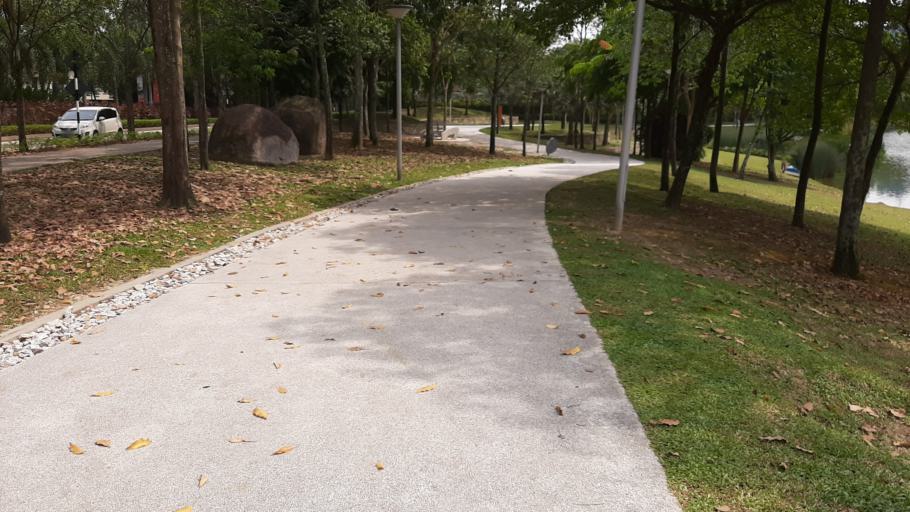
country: MY
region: Kuala Lumpur
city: Kuala Lumpur
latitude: 3.1876
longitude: 101.6293
